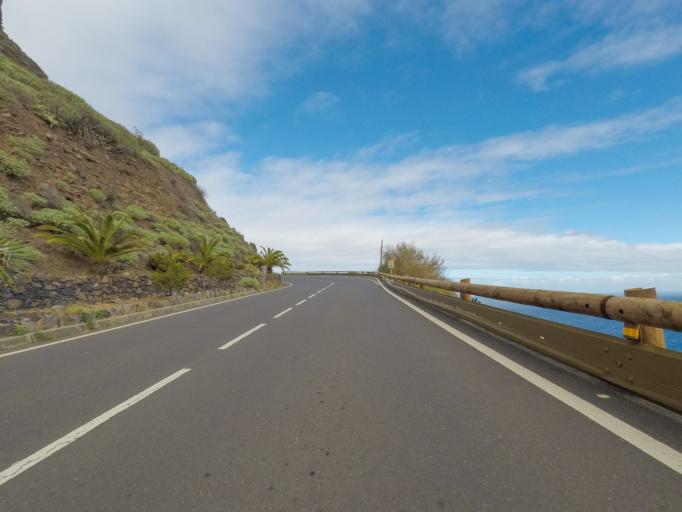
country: ES
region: Canary Islands
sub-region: Provincia de Santa Cruz de Tenerife
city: Agulo
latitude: 28.1828
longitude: -17.1871
